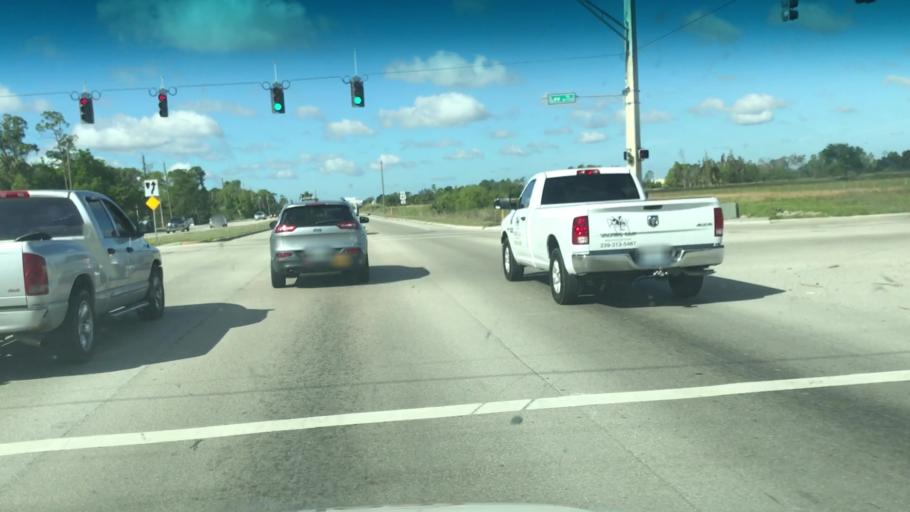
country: US
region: Florida
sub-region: Lee County
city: San Carlos Park
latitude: 26.4929
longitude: -81.8131
